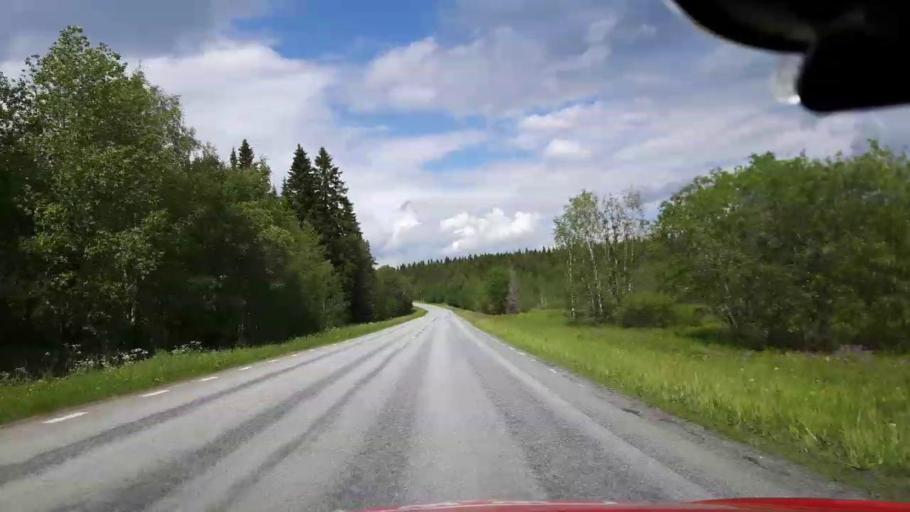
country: SE
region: Jaemtland
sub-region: Krokoms Kommun
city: Krokom
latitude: 63.3735
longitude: 14.3864
